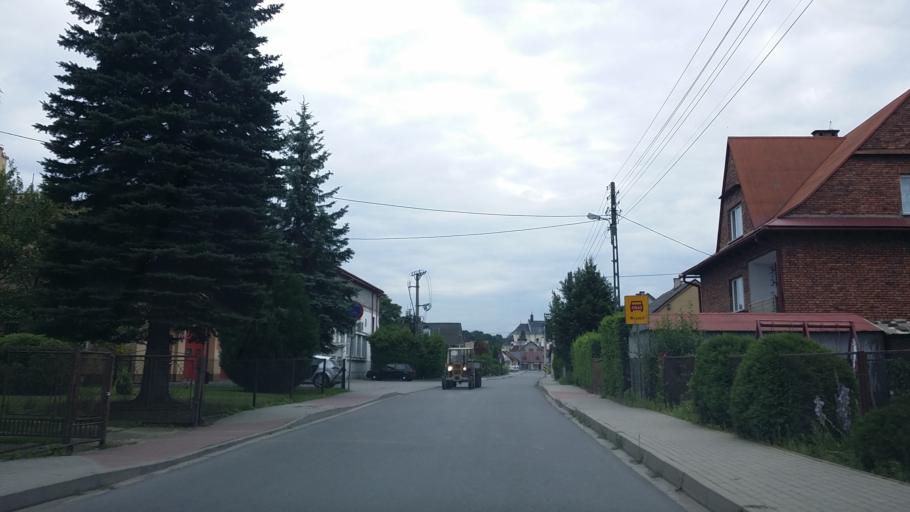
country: PL
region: Lesser Poland Voivodeship
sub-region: Powiat wadowicki
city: Spytkowice
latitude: 49.9988
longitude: 19.5127
